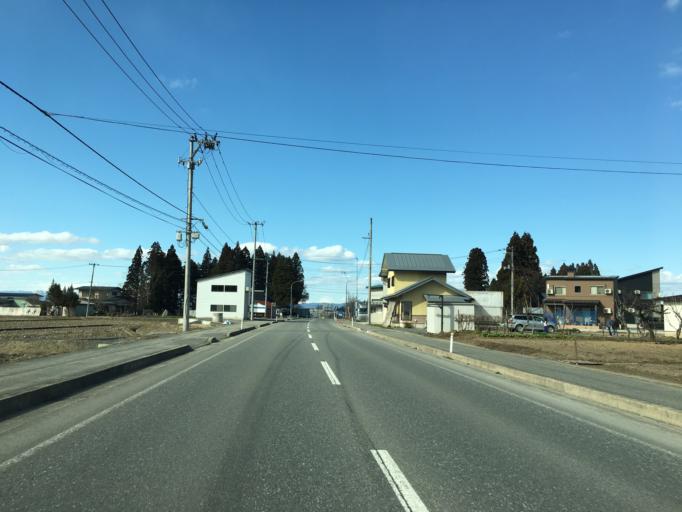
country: JP
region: Yamagata
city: Yonezawa
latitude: 37.9056
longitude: 140.1467
